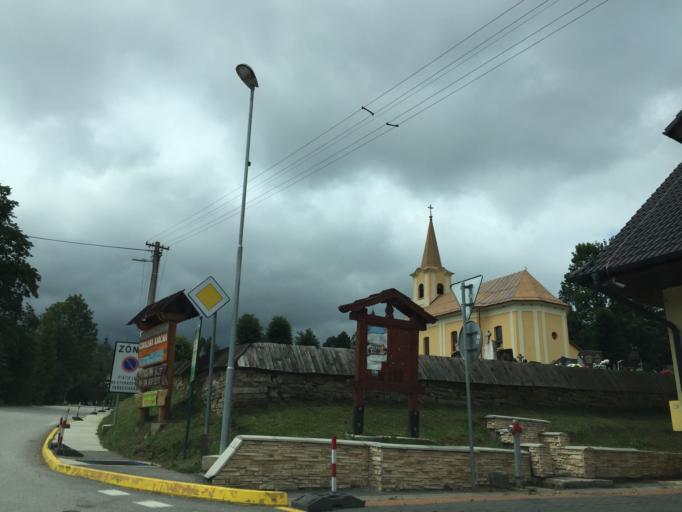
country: SK
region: Presovsky
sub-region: Okres Poprad
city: Zdiar
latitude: 49.2709
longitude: 20.2627
